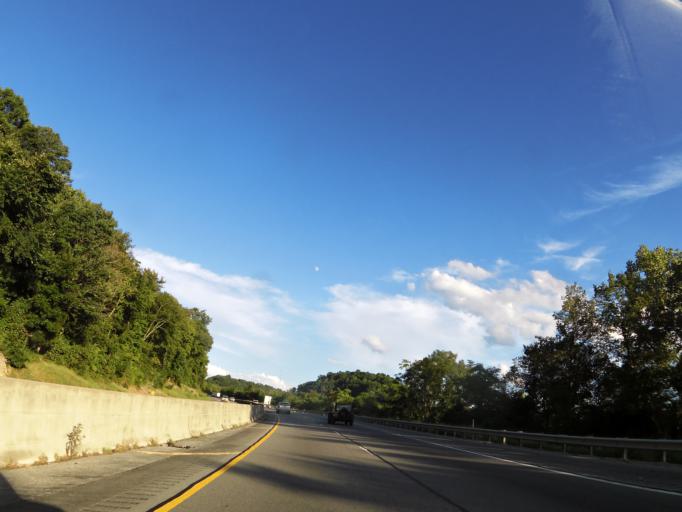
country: US
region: Tennessee
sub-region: Putnam County
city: Lafayette
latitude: 36.1081
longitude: -85.7687
